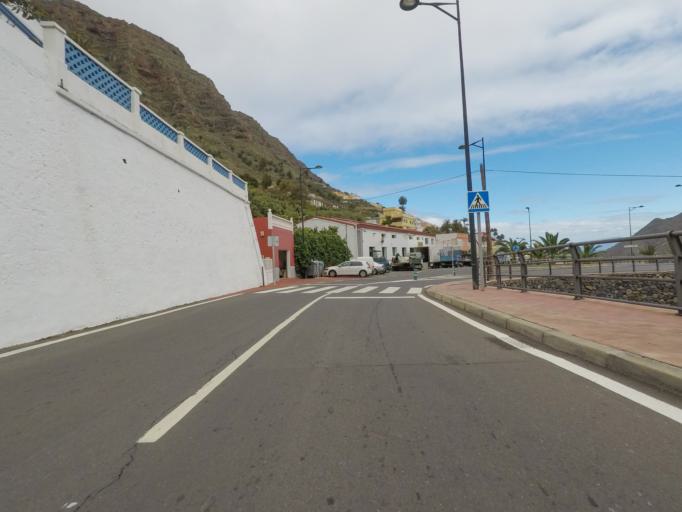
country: ES
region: Canary Islands
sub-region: Provincia de Santa Cruz de Tenerife
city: Hermigua
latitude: 28.1668
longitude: -17.1965
